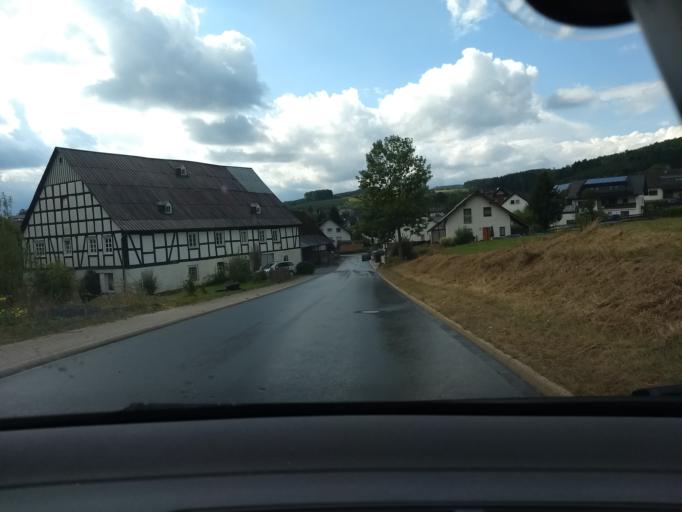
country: DE
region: North Rhine-Westphalia
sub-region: Regierungsbezirk Arnsberg
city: Finnentrop
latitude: 51.1922
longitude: 8.0246
